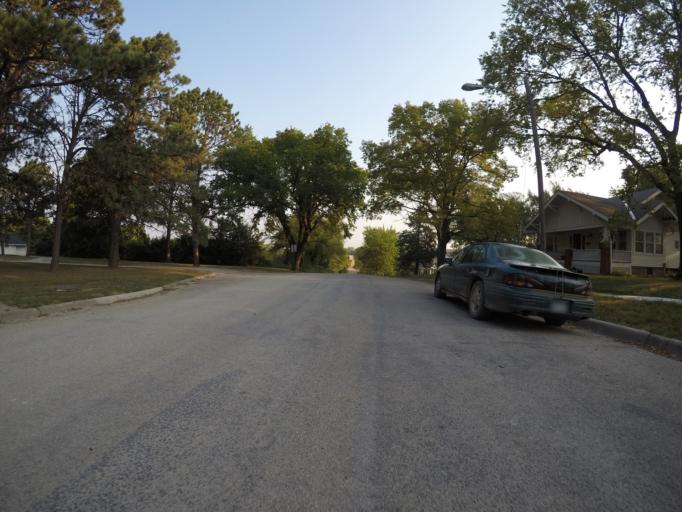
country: US
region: Kansas
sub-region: Marshall County
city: Marysville
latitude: 39.8525
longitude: -96.6481
